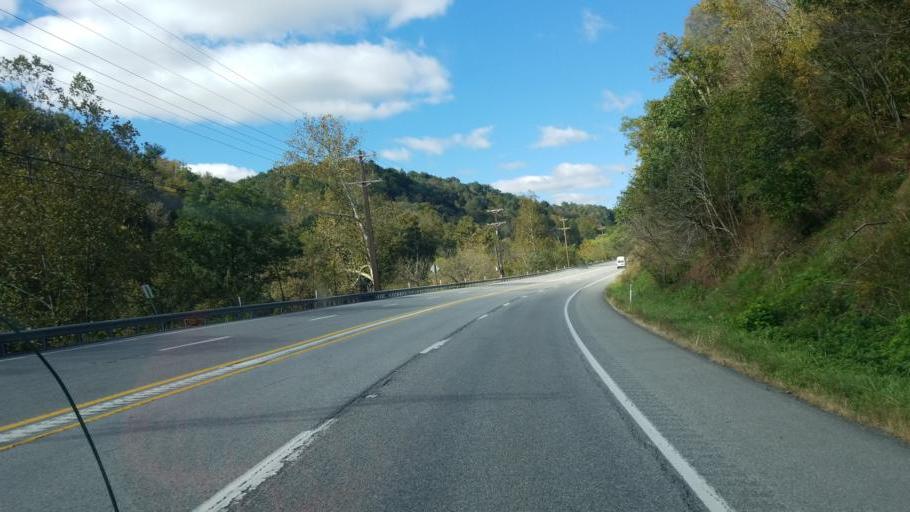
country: US
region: Pennsylvania
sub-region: Bedford County
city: Earlston
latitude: 39.9921
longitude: -78.2732
